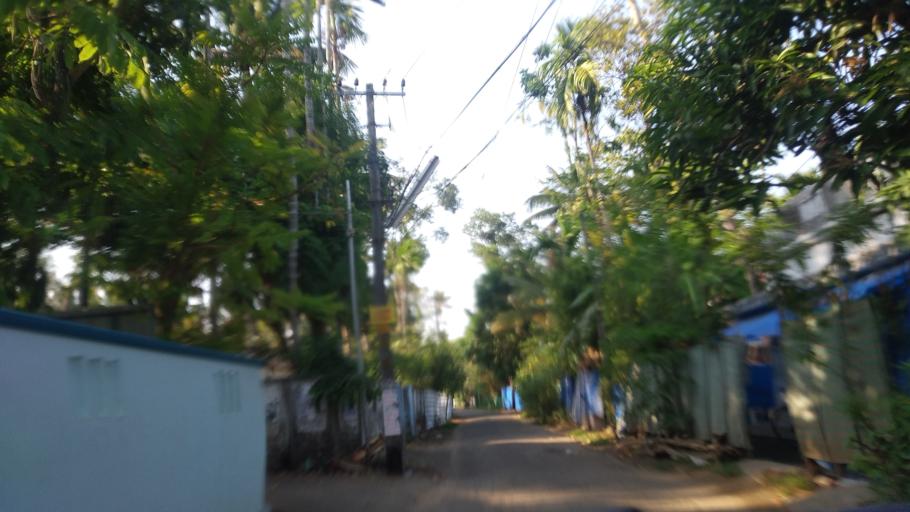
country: IN
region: Kerala
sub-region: Thrissur District
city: Kodungallur
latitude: 10.1372
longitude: 76.2022
